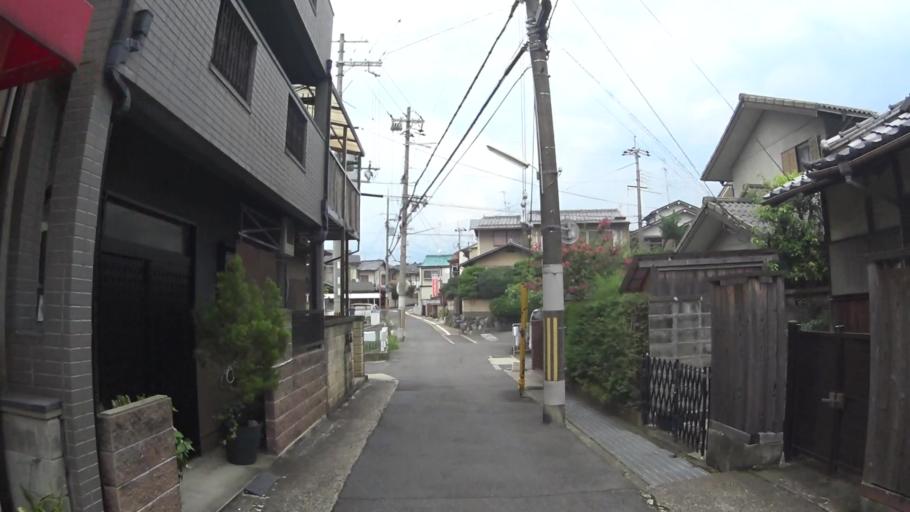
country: JP
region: Kyoto
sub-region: Kyoto-shi
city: Kamigyo-ku
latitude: 35.0481
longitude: 135.7950
